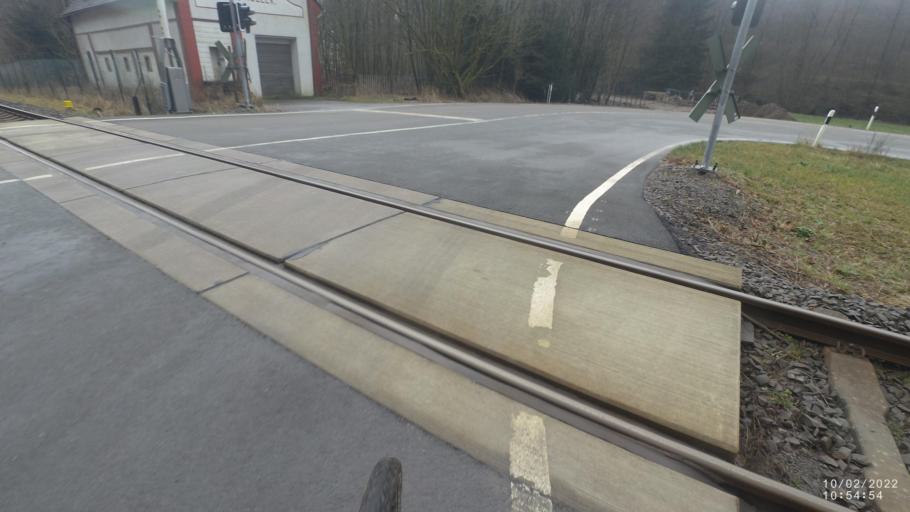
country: DE
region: North Rhine-Westphalia
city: Kierspe
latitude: 51.1602
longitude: 7.5979
